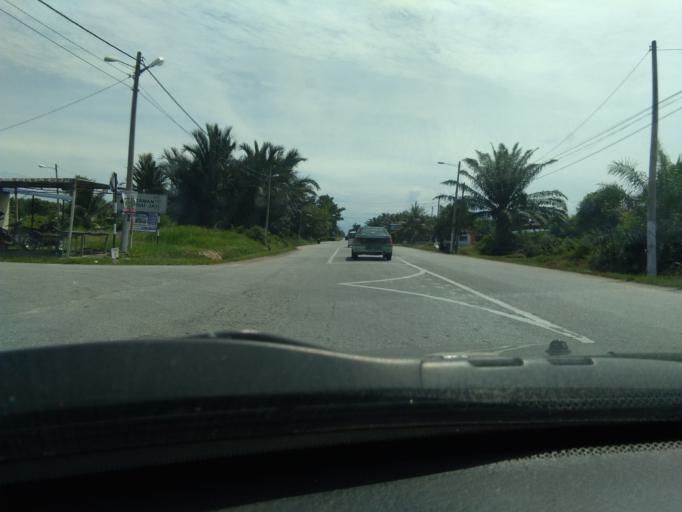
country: MY
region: Perak
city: Bagan Serai
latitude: 5.0213
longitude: 100.5483
